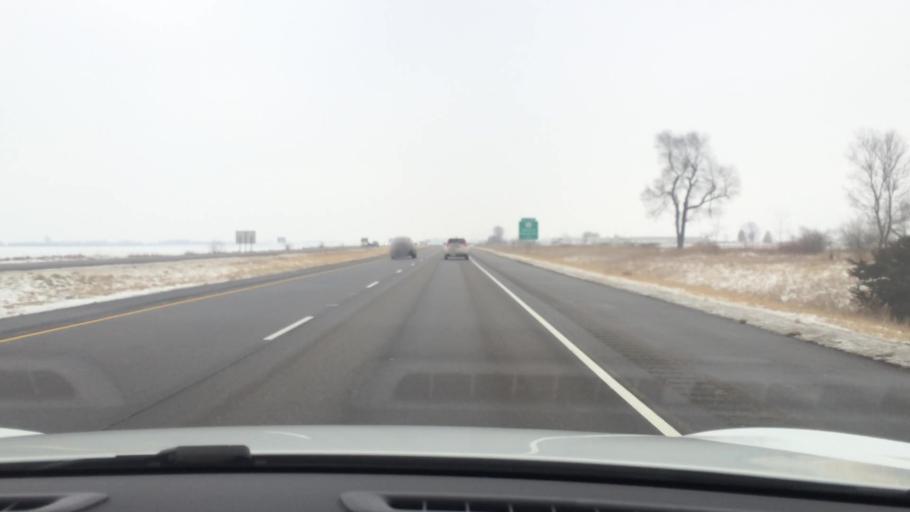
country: US
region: Illinois
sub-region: McLean County
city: Le Roy
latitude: 40.3272
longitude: -88.7453
